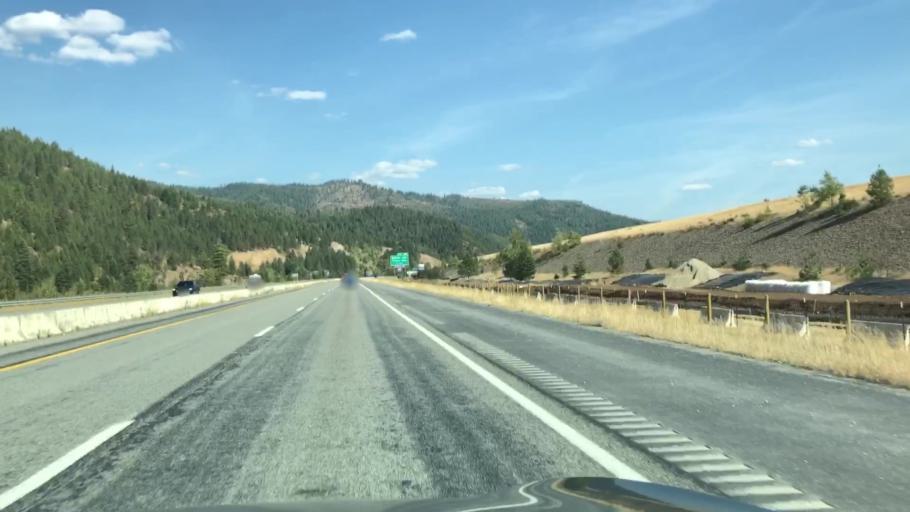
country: US
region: Idaho
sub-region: Shoshone County
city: Kellogg
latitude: 47.5482
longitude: -116.1491
